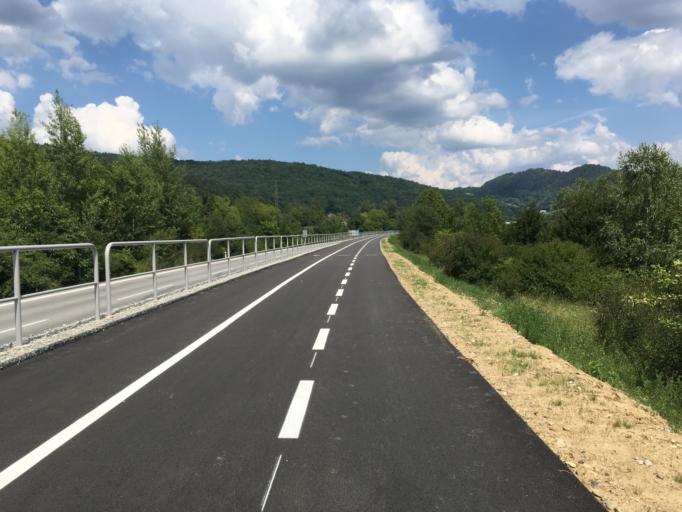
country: SK
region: Nitriansky
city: Puchov
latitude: 49.1336
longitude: 18.3354
